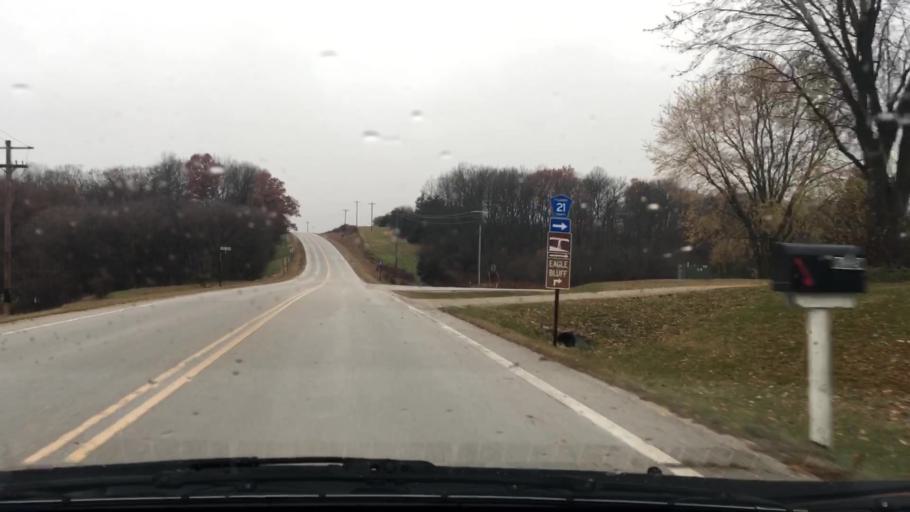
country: US
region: Minnesota
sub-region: Fillmore County
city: Preston
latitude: 43.7337
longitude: -92.0045
